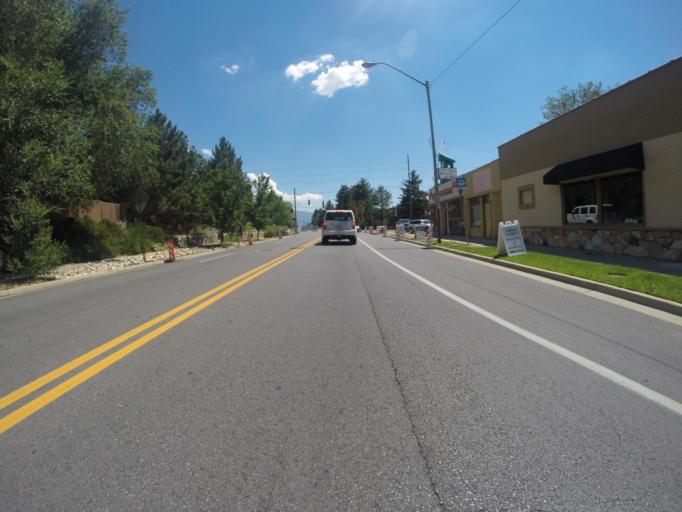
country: US
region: Utah
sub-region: Salt Lake County
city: Willard
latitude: 40.7134
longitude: -111.8556
